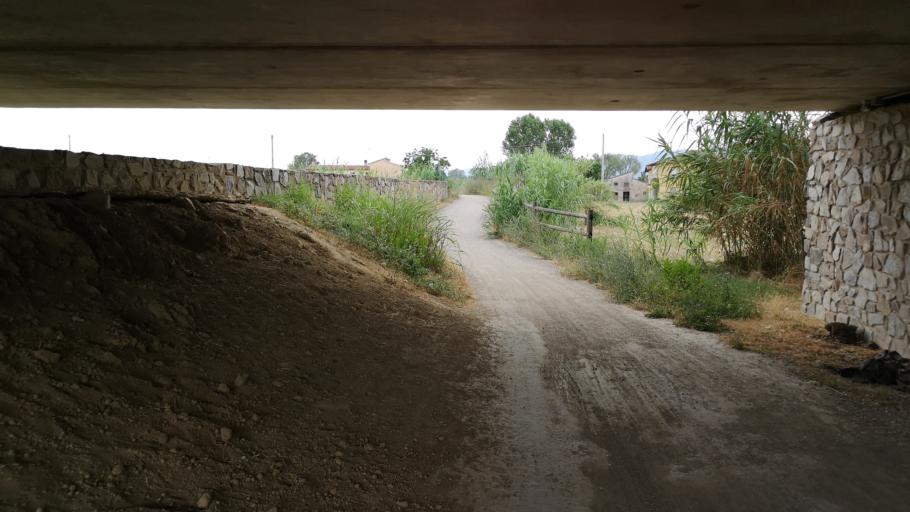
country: IT
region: Tuscany
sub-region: Provincia di Prato
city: Prato
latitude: 43.8791
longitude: 11.0471
